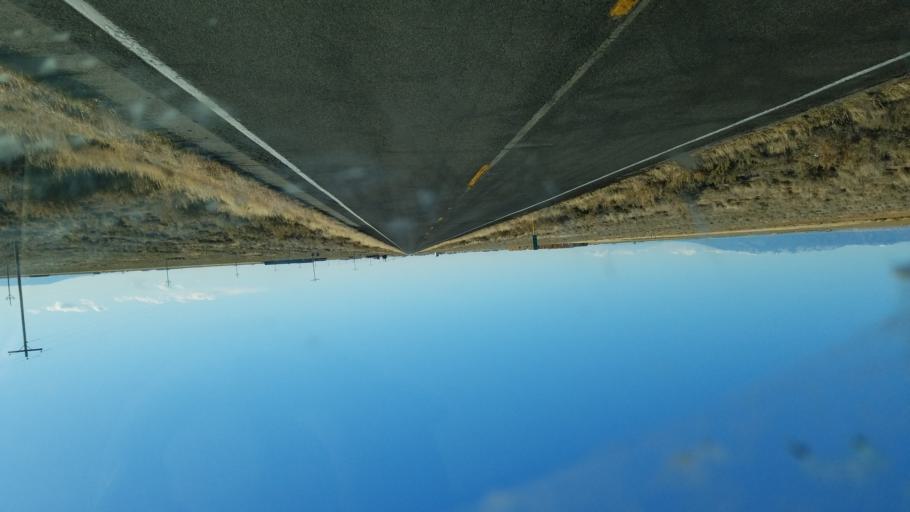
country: US
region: Colorado
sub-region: Saguache County
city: Saguache
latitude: 38.1225
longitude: -105.9222
